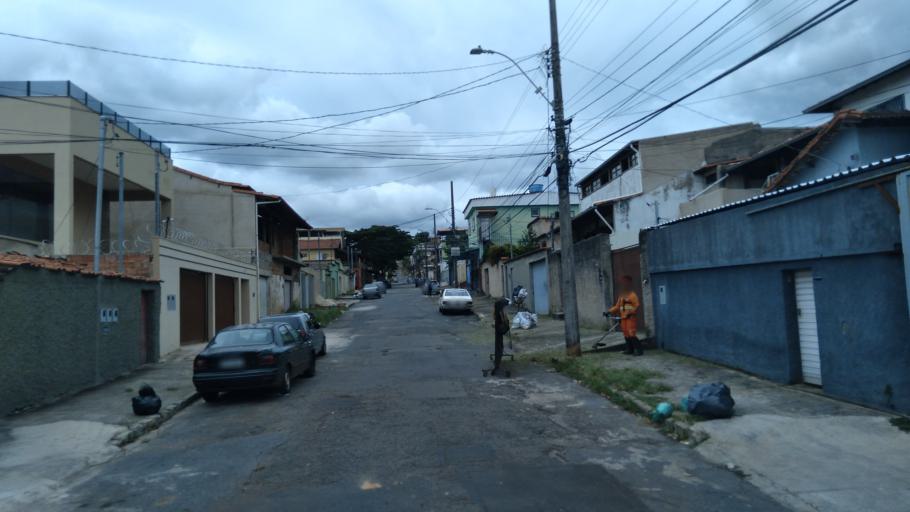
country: BR
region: Minas Gerais
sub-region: Contagem
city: Contagem
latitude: -19.9107
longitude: -44.0034
